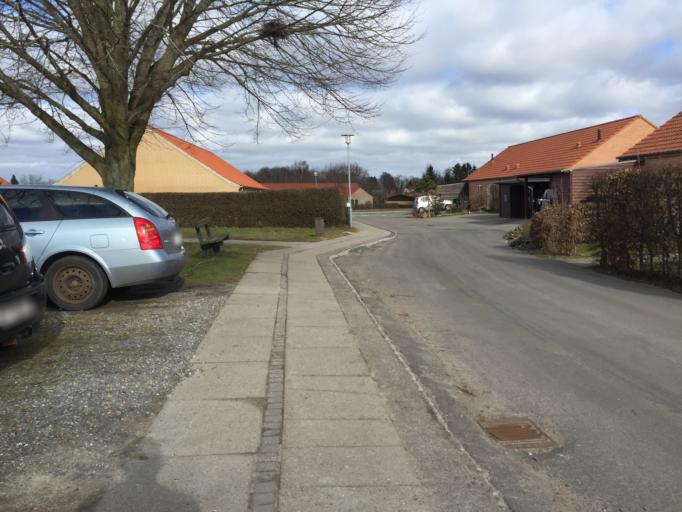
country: DK
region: South Denmark
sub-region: Kerteminde Kommune
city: Langeskov
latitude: 55.3969
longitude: 10.6108
